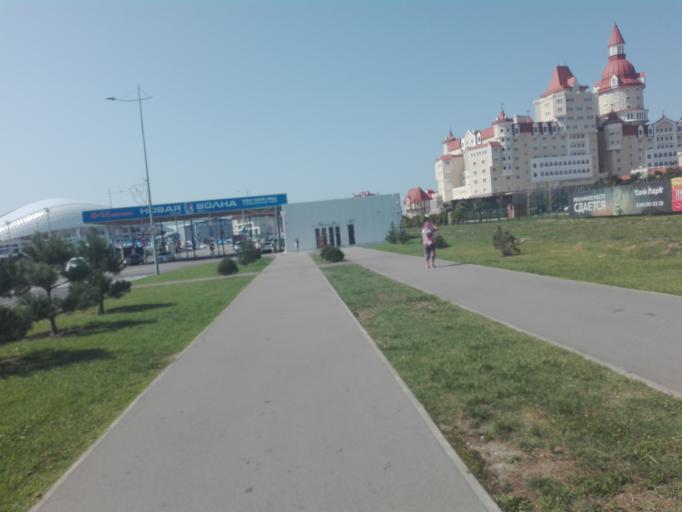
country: RU
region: Krasnodarskiy
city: Adler
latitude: 43.4018
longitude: 39.9655
